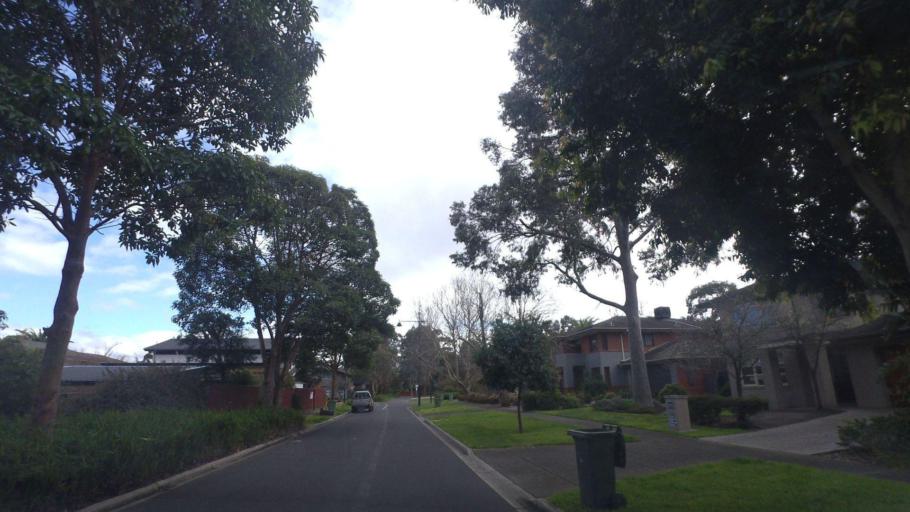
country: AU
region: Victoria
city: Macleod
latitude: -37.7177
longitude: 145.0617
